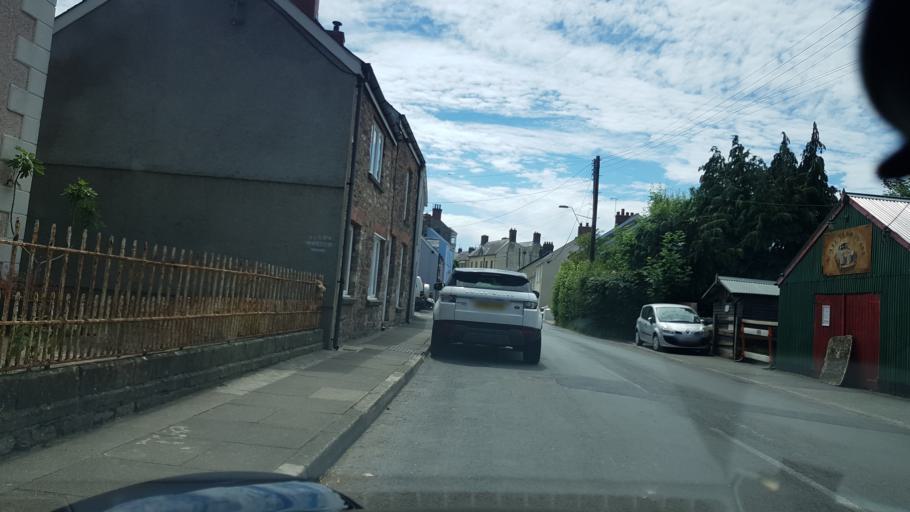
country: GB
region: Wales
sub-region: Carmarthenshire
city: Saint Clears
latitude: 51.7739
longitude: -4.4630
